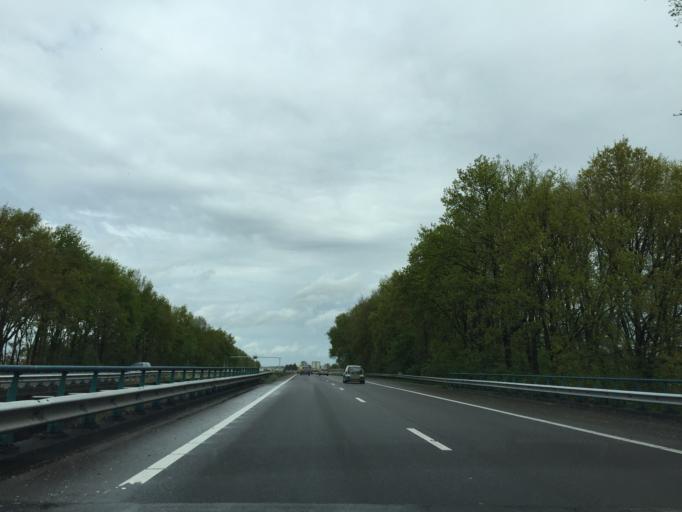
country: NL
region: Gelderland
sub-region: Gemeente Ermelo
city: Horst
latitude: 52.2664
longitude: 5.5352
